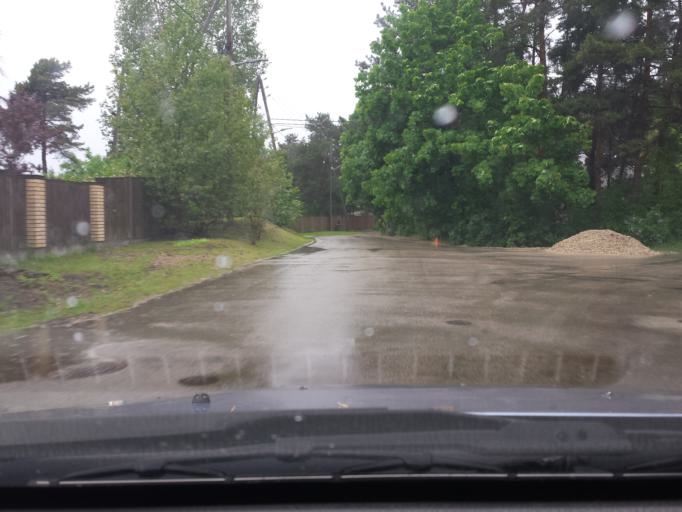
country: LV
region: Riga
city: Bolderaja
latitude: 57.0715
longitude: 24.0993
